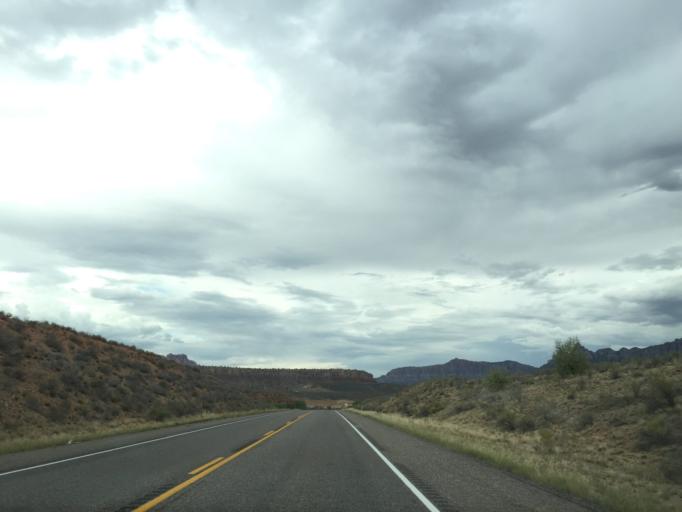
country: US
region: Utah
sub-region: Washington County
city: LaVerkin
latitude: 37.1714
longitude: -113.0869
